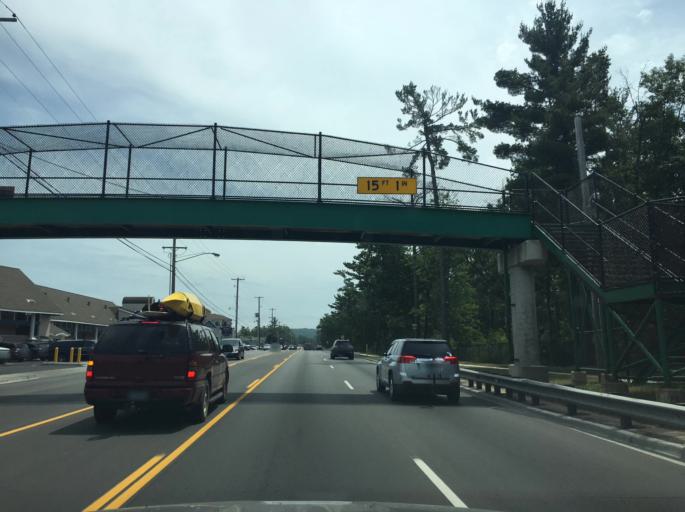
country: US
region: Michigan
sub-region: Grand Traverse County
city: Traverse City
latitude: 44.7477
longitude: -85.5519
